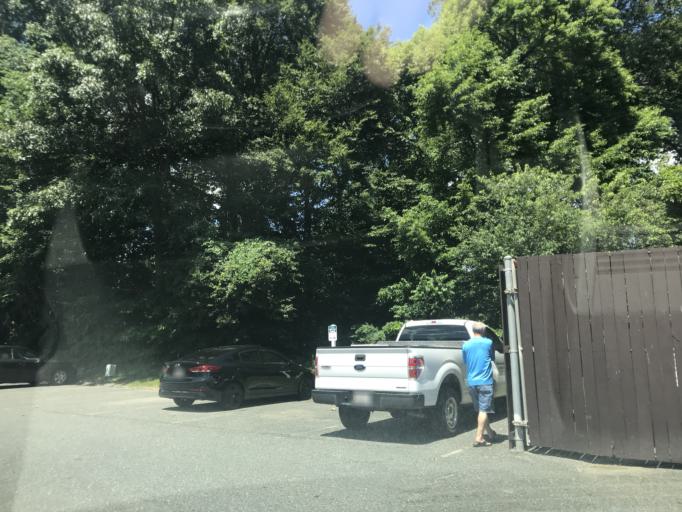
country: US
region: Maryland
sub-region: Harford County
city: Bel Air
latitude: 39.5254
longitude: -76.3456
